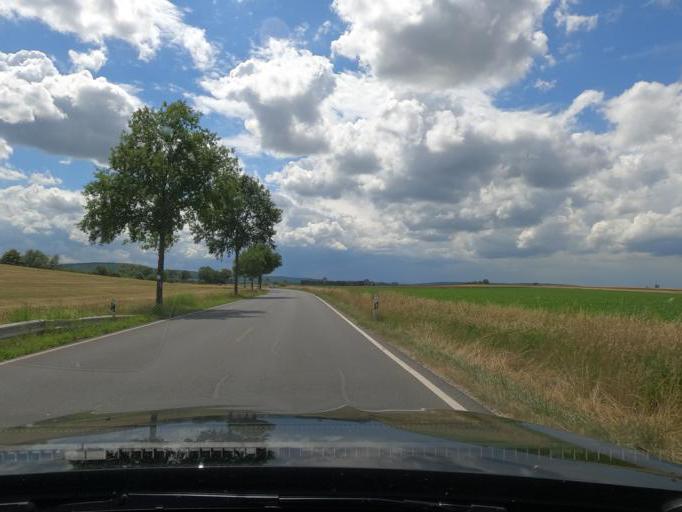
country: DE
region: Lower Saxony
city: Lengede
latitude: 52.1600
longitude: 10.2964
